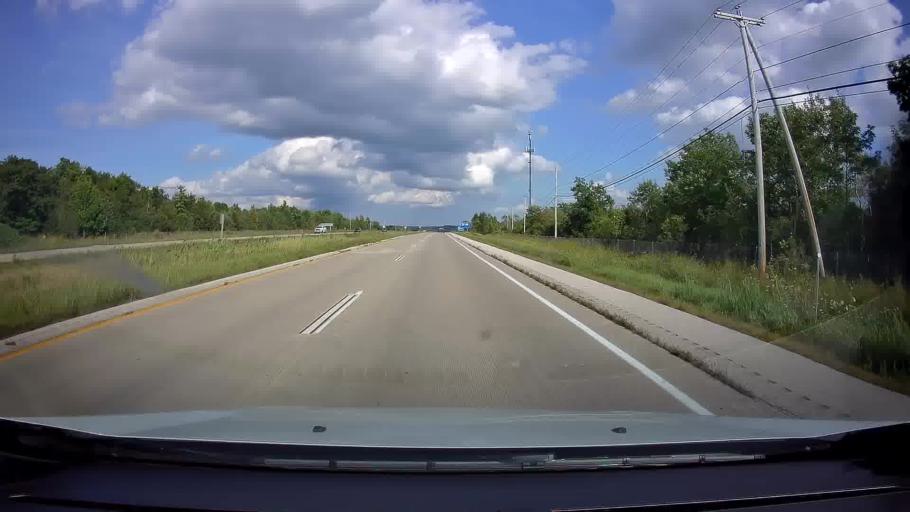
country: US
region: Wisconsin
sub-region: Kewaunee County
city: Luxemburg
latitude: 44.6337
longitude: -87.7945
